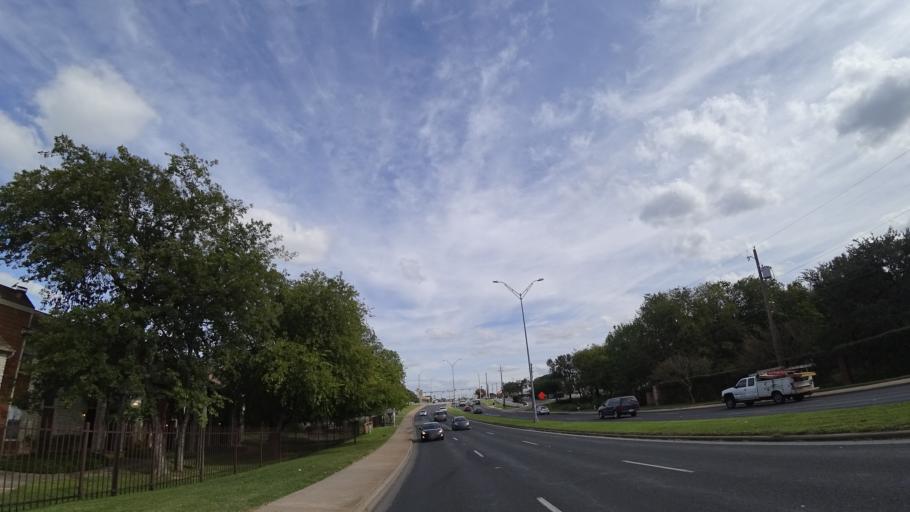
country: US
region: Texas
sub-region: Travis County
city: Onion Creek
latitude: 30.1919
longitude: -97.7748
